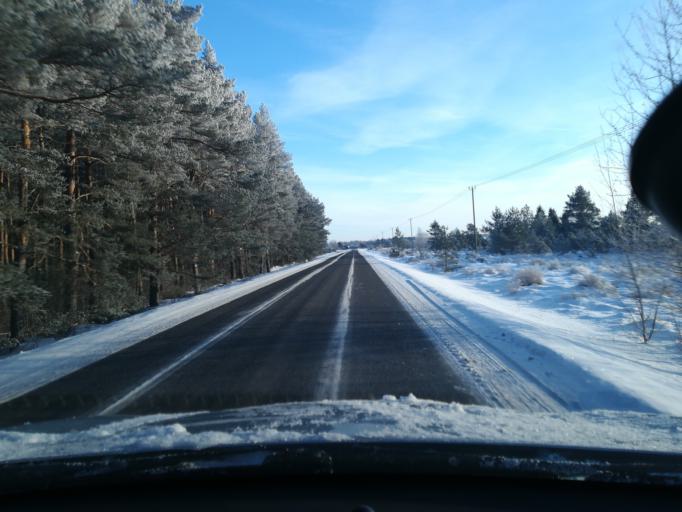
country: EE
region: Harju
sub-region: Keila linn
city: Keila
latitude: 59.3920
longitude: 24.3913
